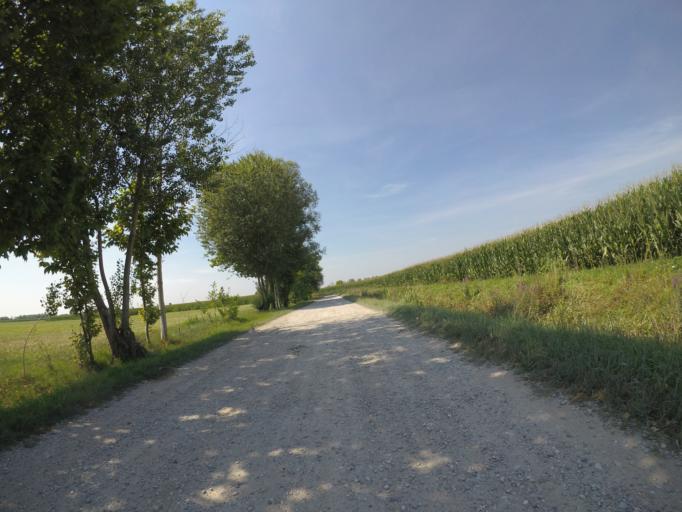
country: IT
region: Friuli Venezia Giulia
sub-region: Provincia di Udine
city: Varmo
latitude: 45.9136
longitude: 12.9897
